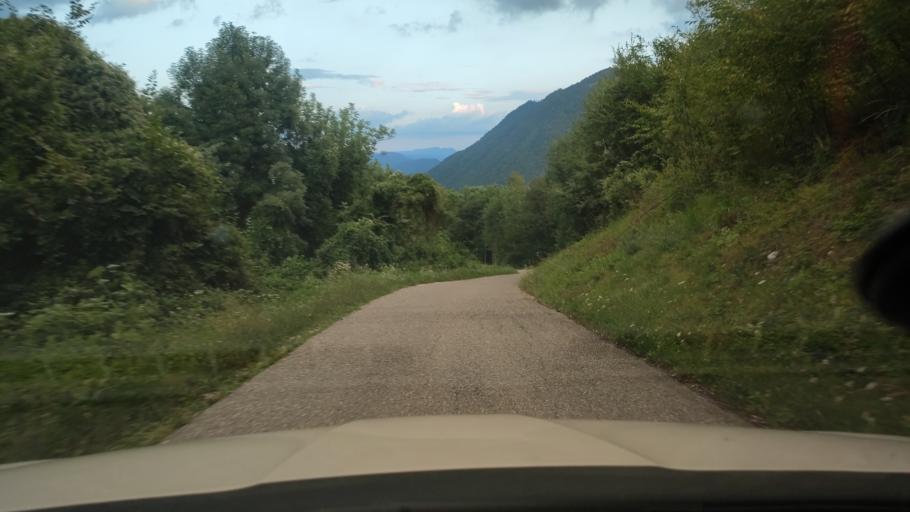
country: IT
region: Friuli Venezia Giulia
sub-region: Provincia di Udine
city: Cras
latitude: 46.2187
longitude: 13.6431
